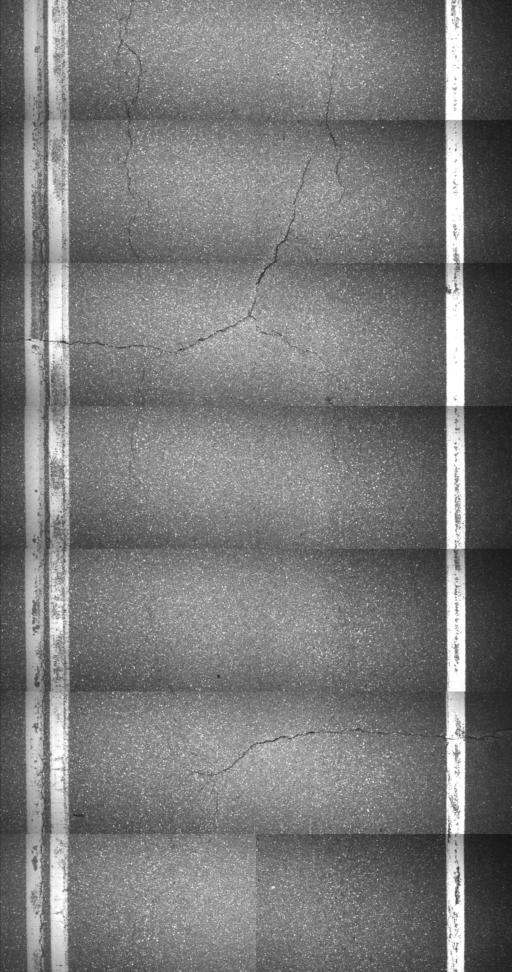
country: US
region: New Hampshire
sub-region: Coos County
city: Stratford
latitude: 44.7305
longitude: -71.6356
